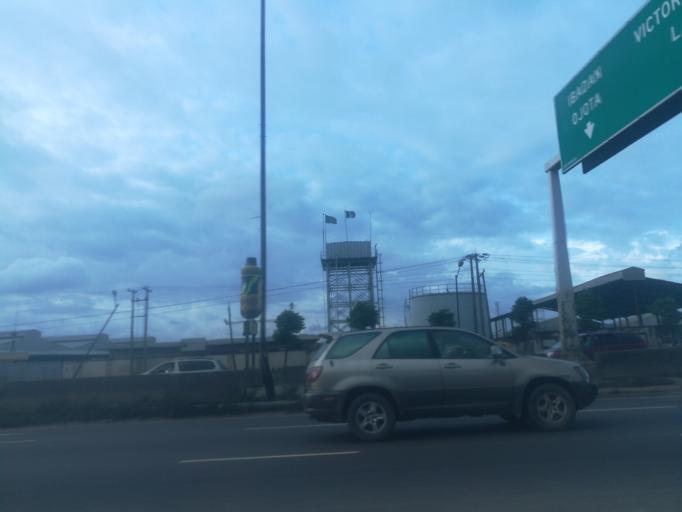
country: NG
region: Lagos
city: Somolu
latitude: 6.5476
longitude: 3.3832
